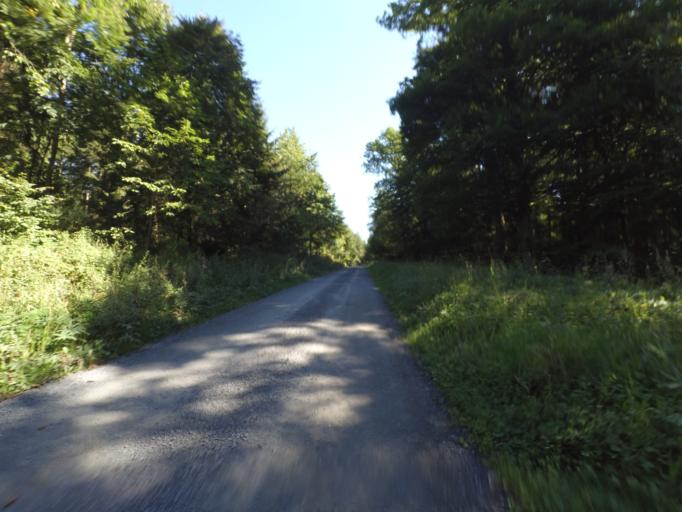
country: DE
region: Rheinland-Pfalz
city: Horscheid
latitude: 50.2055
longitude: 6.8588
